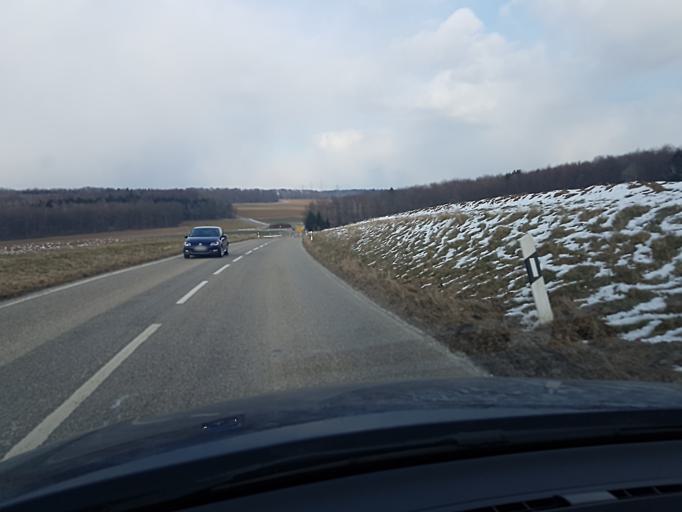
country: DE
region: Baden-Wuerttemberg
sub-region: Regierungsbezirk Stuttgart
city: Eberdingen
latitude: 48.8609
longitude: 8.9858
